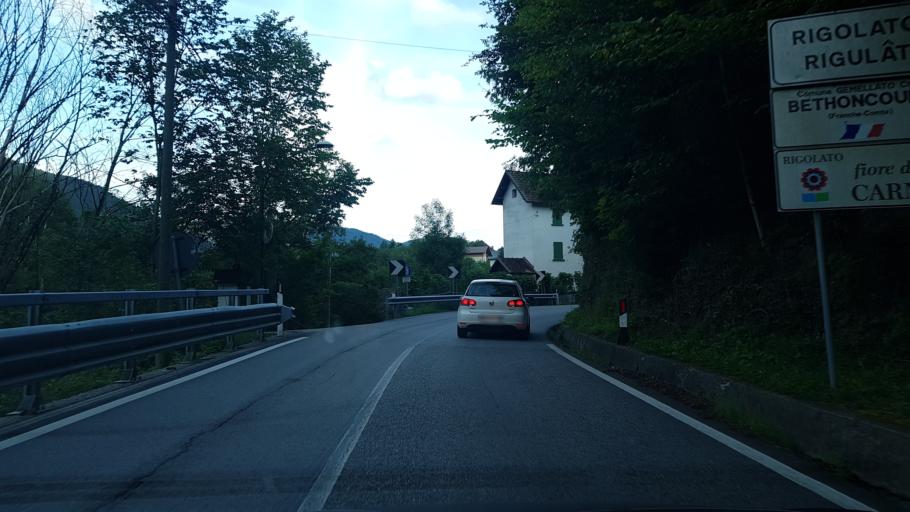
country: IT
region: Friuli Venezia Giulia
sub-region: Provincia di Udine
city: Rigolato
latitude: 46.5569
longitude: 12.8489
